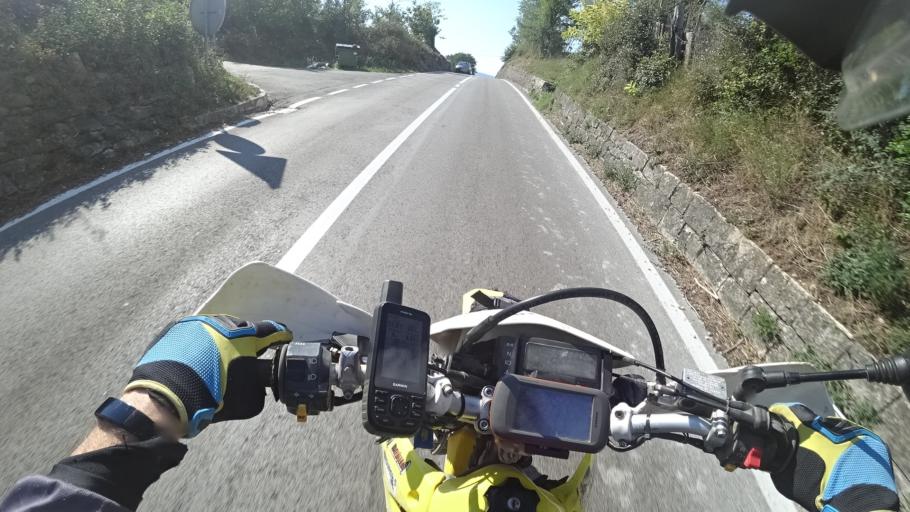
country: HR
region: Sibensko-Kniniska
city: Knin
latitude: 44.0153
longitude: 16.1968
